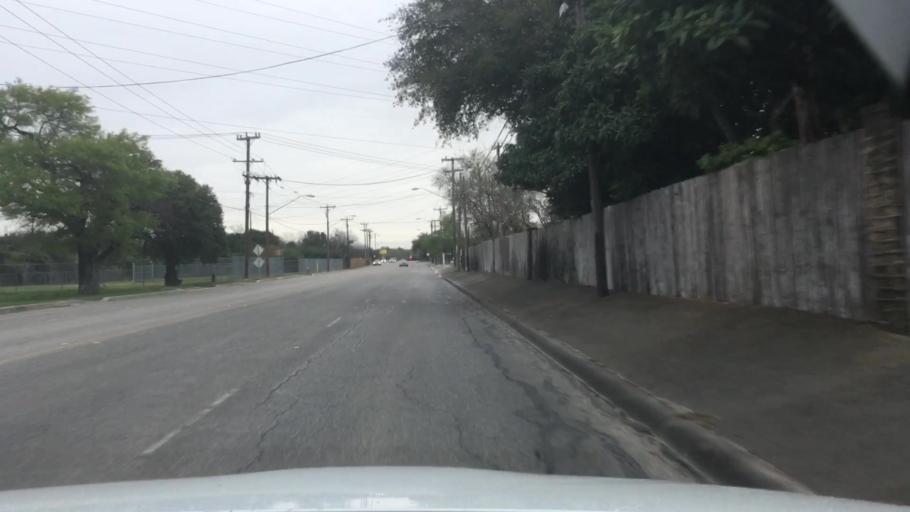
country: US
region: Texas
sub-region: Bexar County
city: Windcrest
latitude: 29.5230
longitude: -98.3857
